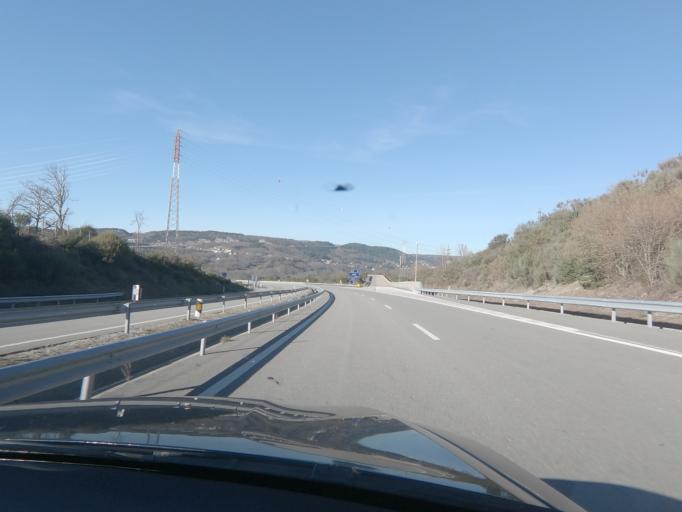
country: PT
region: Vila Real
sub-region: Vila Pouca de Aguiar
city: Vila Pouca de Aguiar
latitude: 41.4748
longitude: -7.6438
